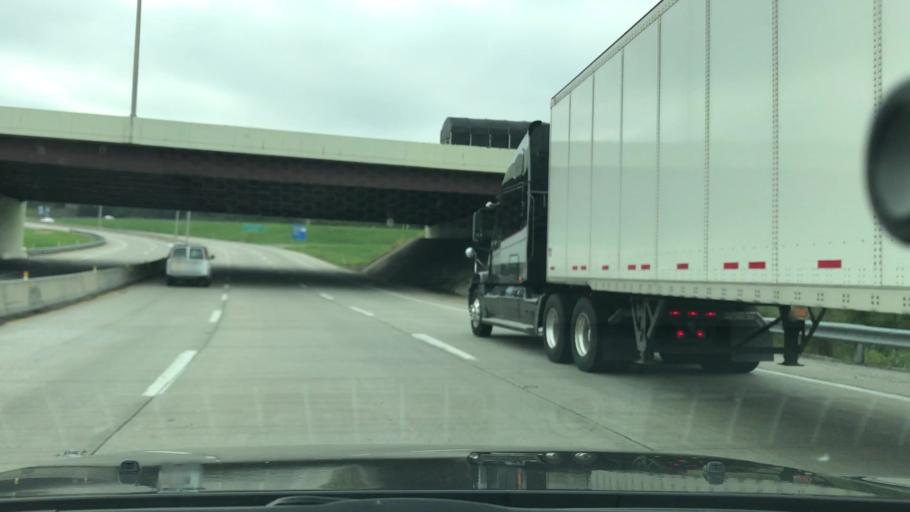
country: US
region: Pennsylvania
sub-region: Montgomery County
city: King of Prussia
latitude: 40.0923
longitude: -75.4095
